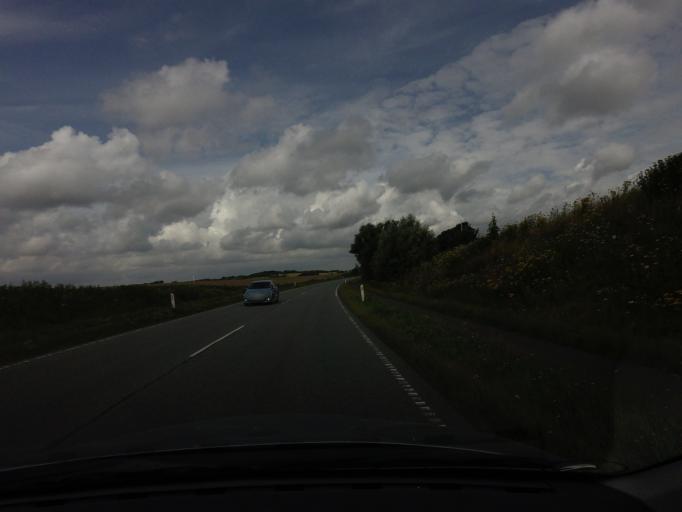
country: DK
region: North Denmark
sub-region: Hjorring Kommune
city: Tars
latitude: 57.3691
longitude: 10.1767
